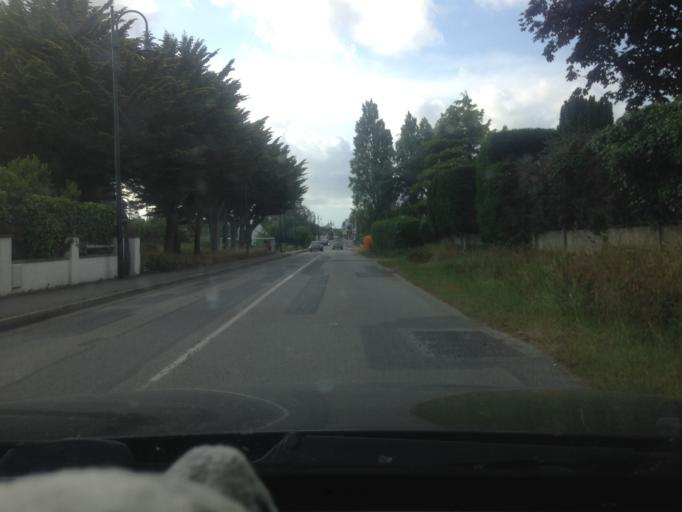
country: FR
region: Brittany
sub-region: Departement du Morbihan
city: Carnac
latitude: 47.5875
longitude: -3.0891
